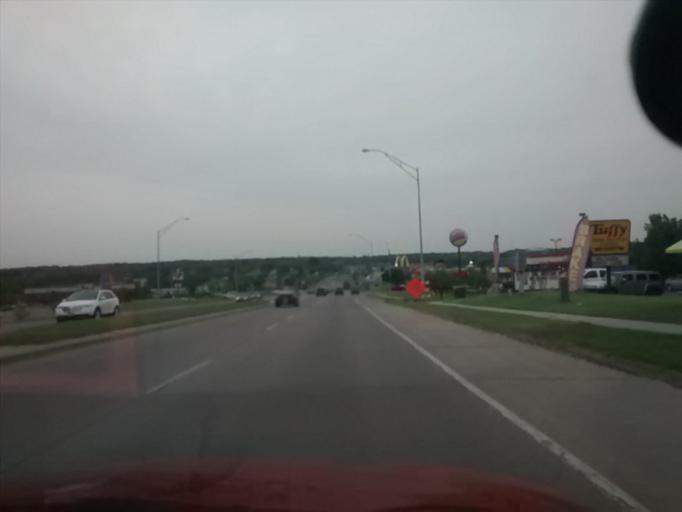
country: US
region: Nebraska
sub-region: Sarpy County
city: Offutt Air Force Base
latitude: 41.1592
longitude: -95.9448
